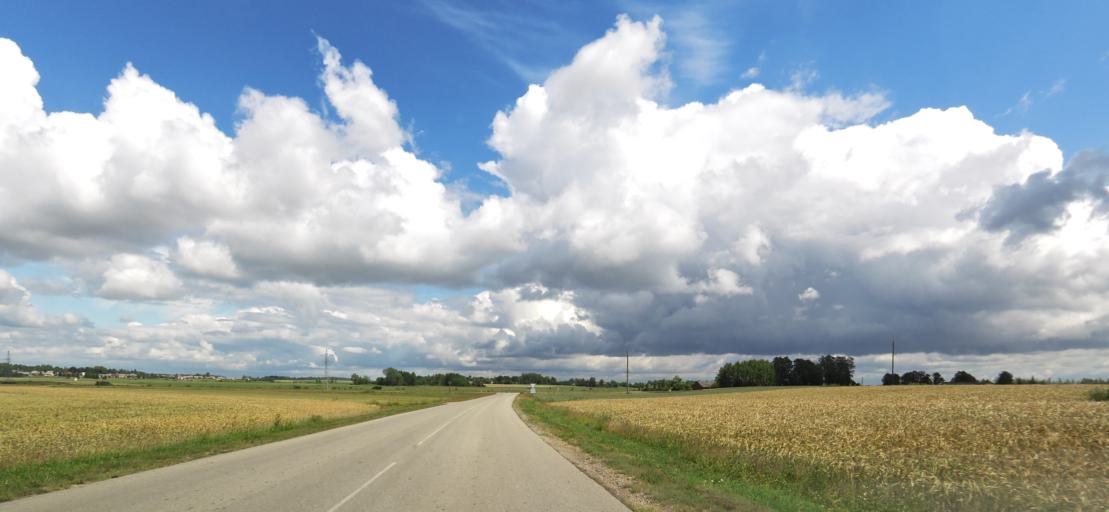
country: LT
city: Vabalninkas
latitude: 55.8925
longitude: 24.8012
